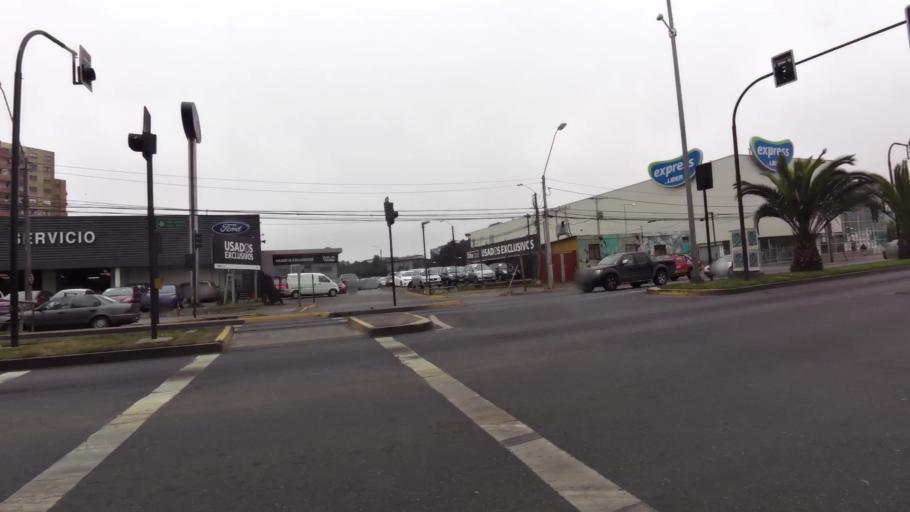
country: CL
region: Biobio
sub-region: Provincia de Concepcion
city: Concepcion
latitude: -36.8138
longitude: -73.0483
